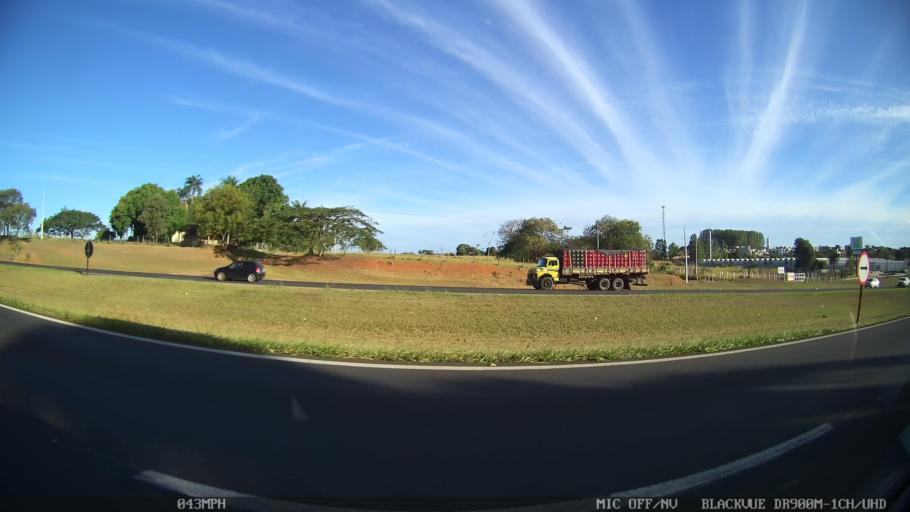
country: BR
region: Sao Paulo
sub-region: Sao Jose Do Rio Preto
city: Sao Jose do Rio Preto
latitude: -20.8160
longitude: -49.4452
